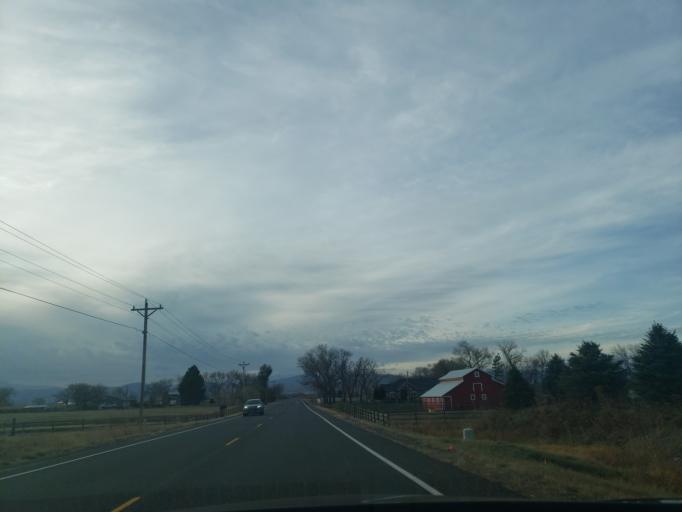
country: US
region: Colorado
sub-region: Larimer County
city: Loveland
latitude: 40.4646
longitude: -105.0008
